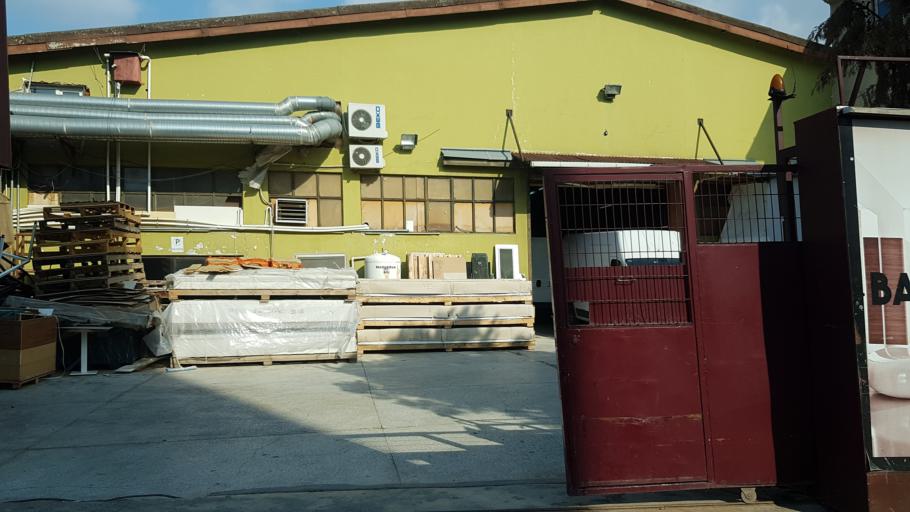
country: TR
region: Istanbul
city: Maltepe
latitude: 40.9045
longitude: 29.1966
